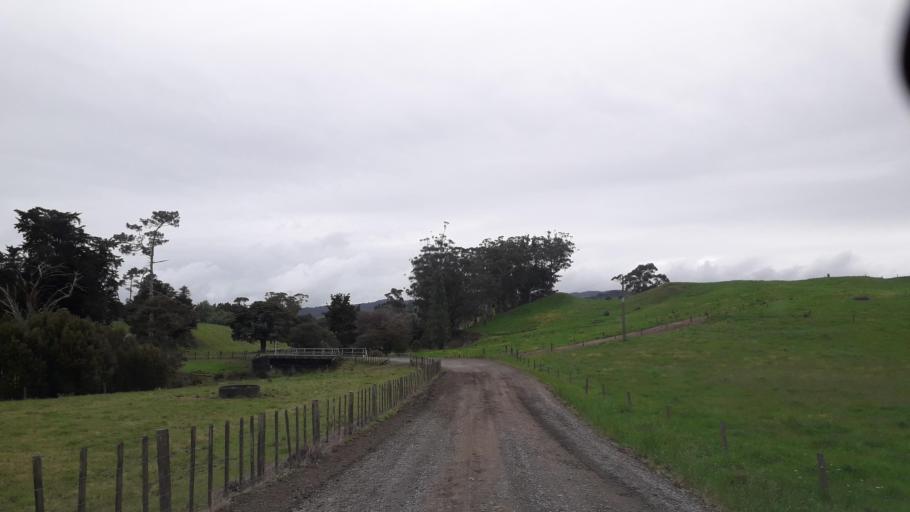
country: NZ
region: Northland
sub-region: Far North District
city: Waimate North
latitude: -35.2994
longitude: 173.5653
